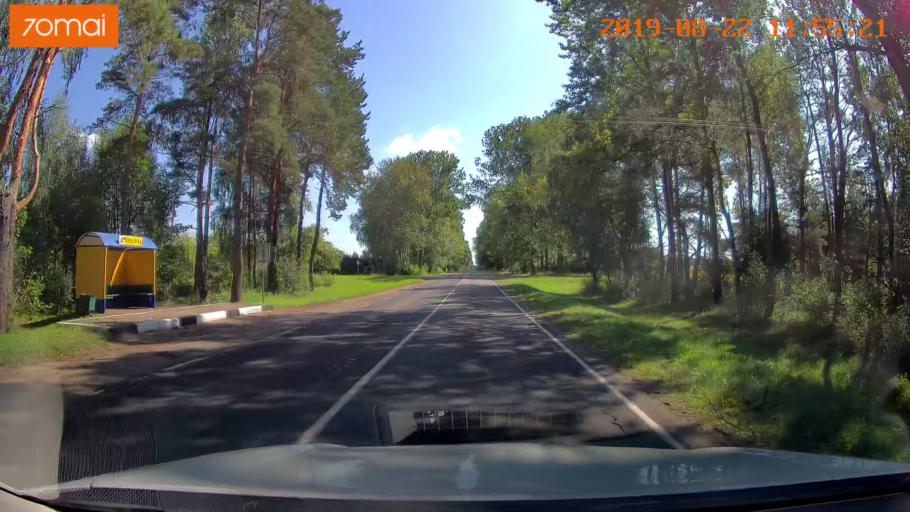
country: BY
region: Minsk
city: Prawdzinski
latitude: 53.4319
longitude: 27.5457
